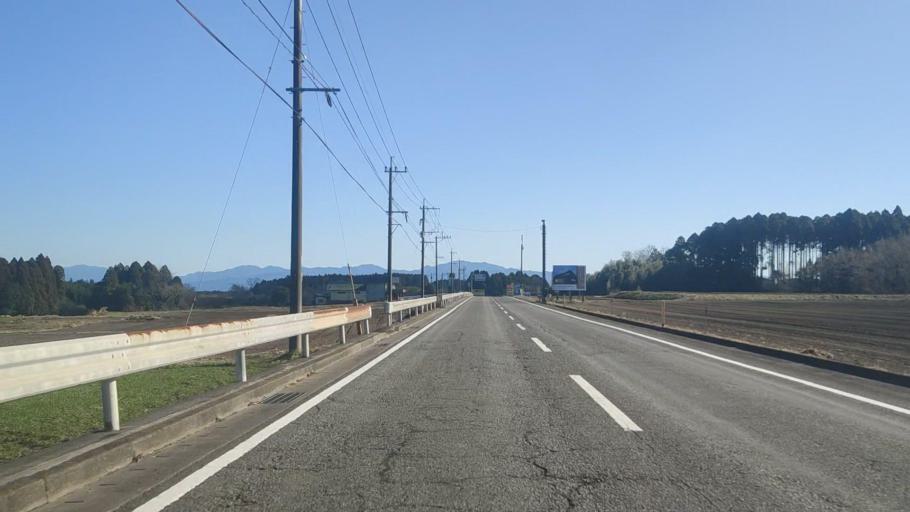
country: JP
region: Kagoshima
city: Sueyoshicho-ninokata
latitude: 31.6884
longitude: 130.9572
